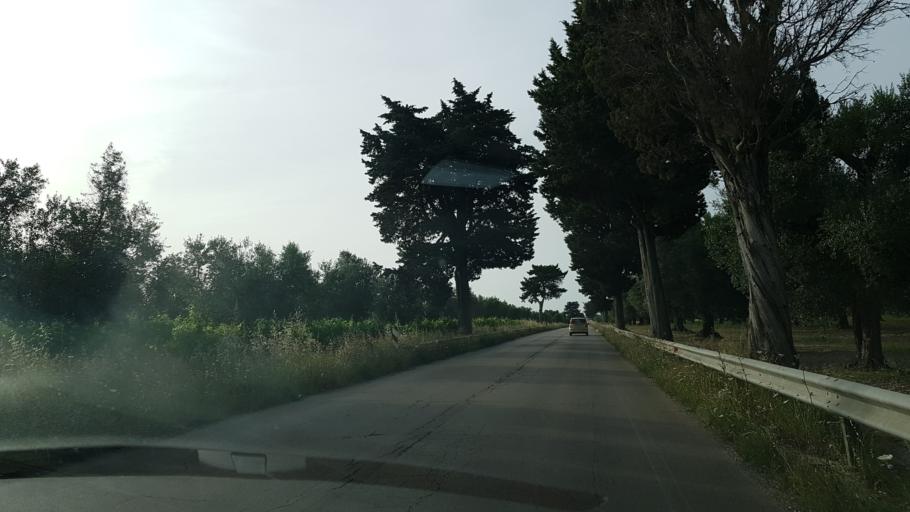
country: IT
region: Apulia
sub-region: Provincia di Brindisi
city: Tuturano
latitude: 40.5271
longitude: 17.9840
